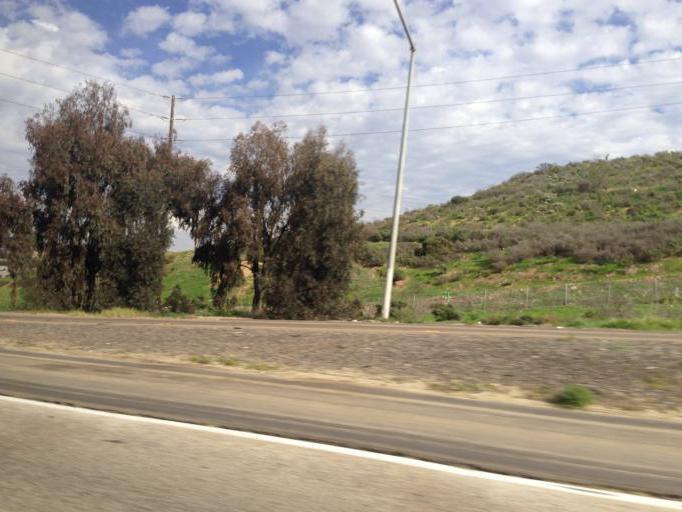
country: US
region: California
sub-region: San Diego County
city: Bonita
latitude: 32.5867
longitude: -117.0363
